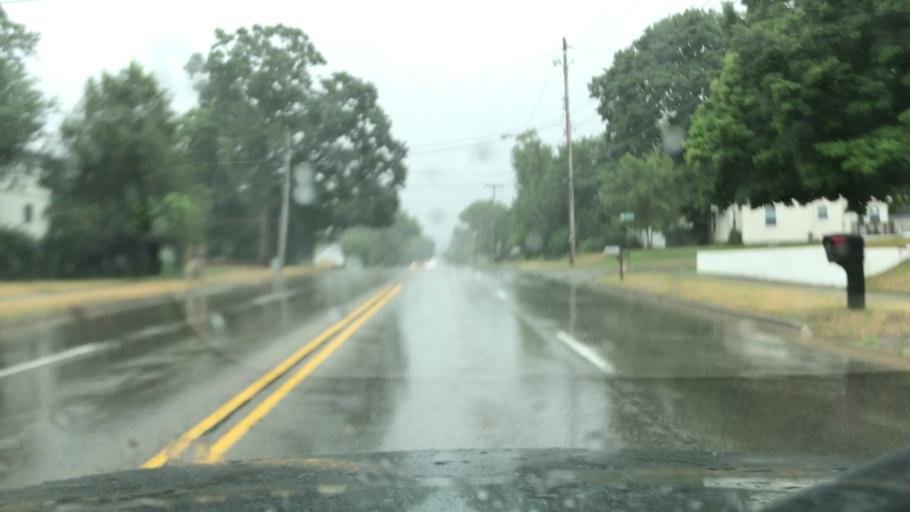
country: US
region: Michigan
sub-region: Kent County
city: Wyoming
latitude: 42.9097
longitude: -85.7248
